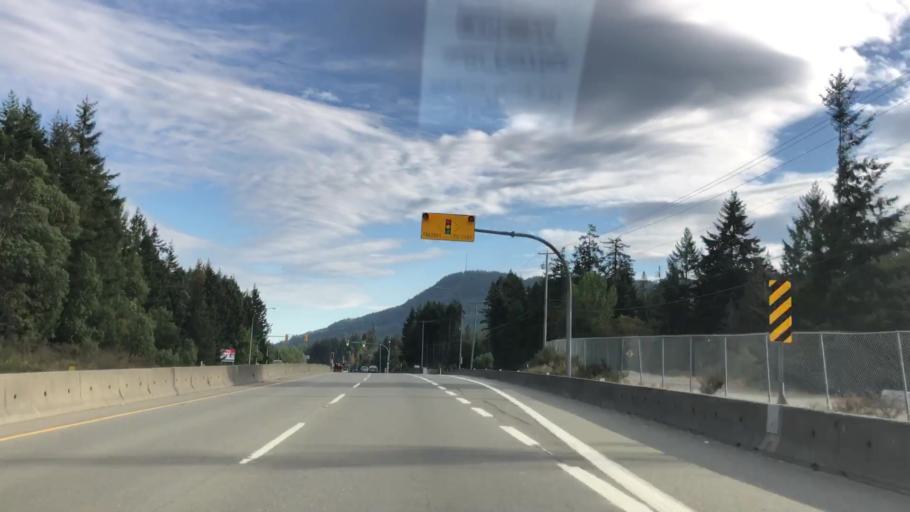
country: CA
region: British Columbia
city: North Saanich
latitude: 48.6288
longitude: -123.5487
